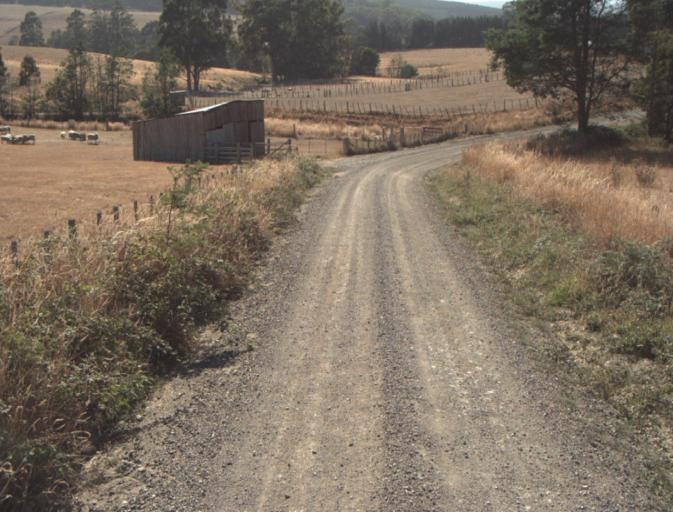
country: AU
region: Tasmania
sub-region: Launceston
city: Mayfield
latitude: -41.1714
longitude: 147.2059
